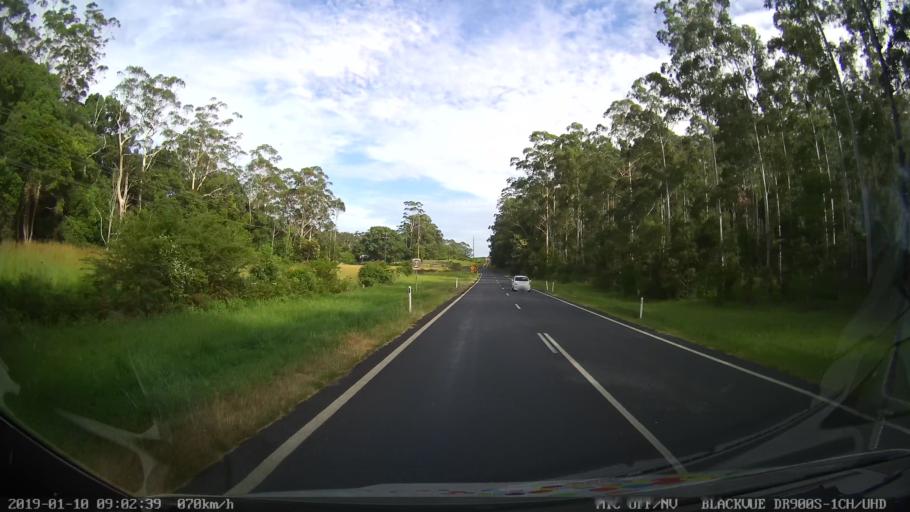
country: AU
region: New South Wales
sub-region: Coffs Harbour
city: Coffs Harbour
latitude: -30.2706
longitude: 153.0516
